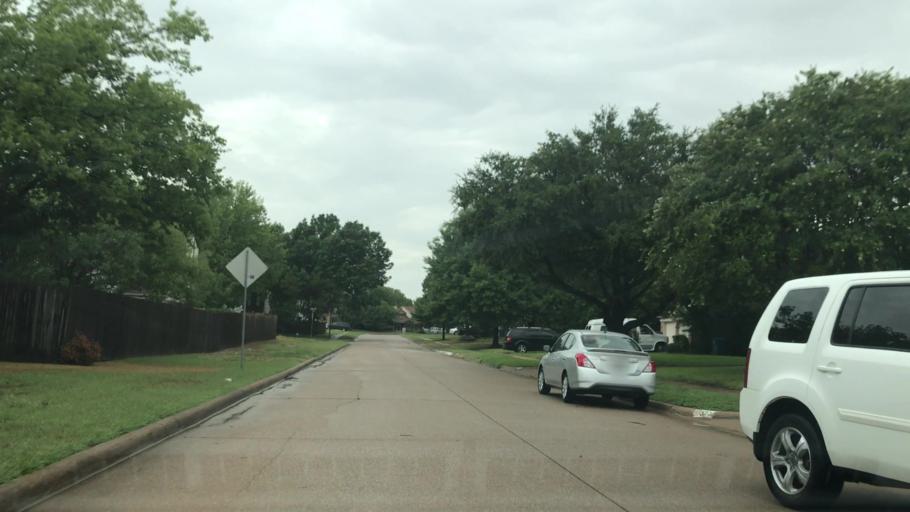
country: US
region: Texas
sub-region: Denton County
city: Flower Mound
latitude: 33.0373
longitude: -97.0551
